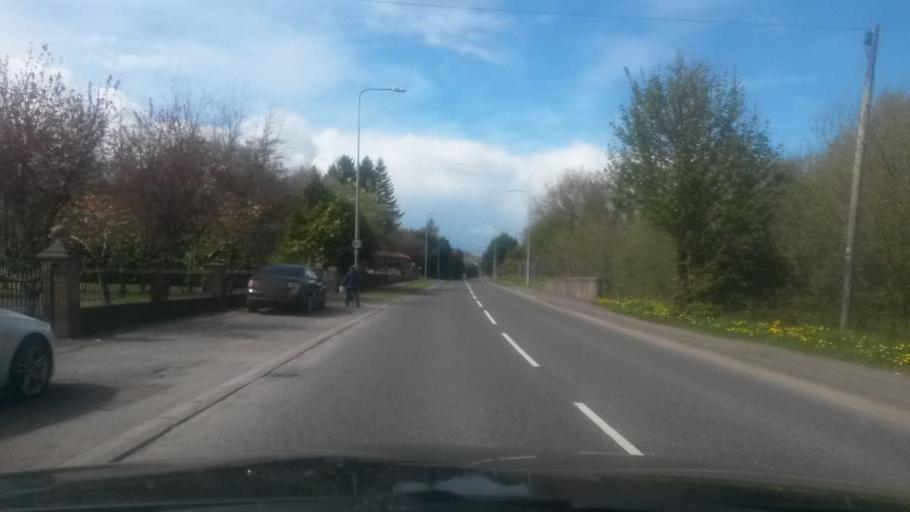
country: GB
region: Northern Ireland
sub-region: Fermanagh District
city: Enniskillen
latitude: 54.3554
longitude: -7.6668
